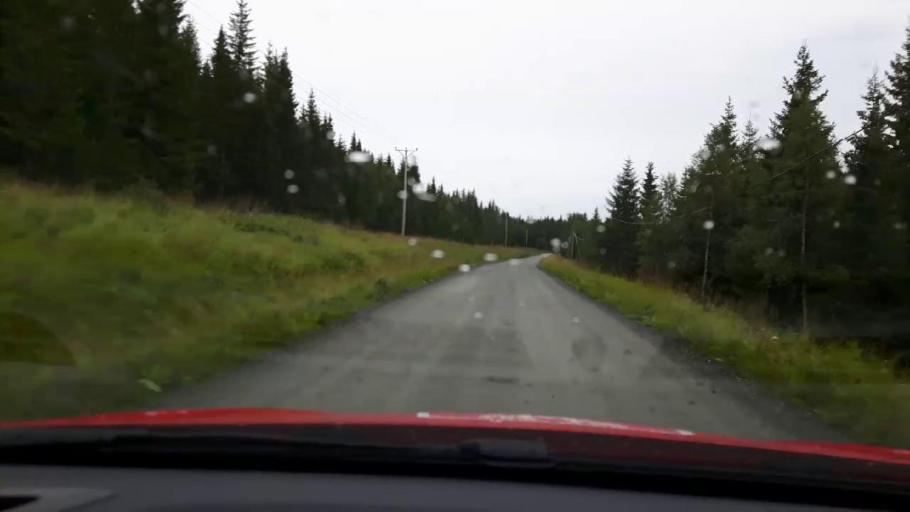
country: SE
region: Jaemtland
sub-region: Are Kommun
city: Are
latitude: 63.4115
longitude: 12.8293
